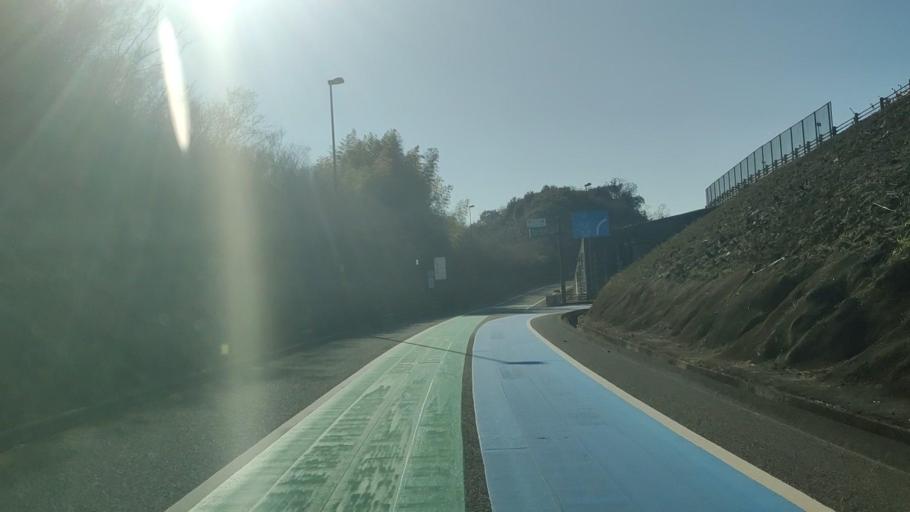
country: JP
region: Oita
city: Oita
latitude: 33.0713
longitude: 131.6296
